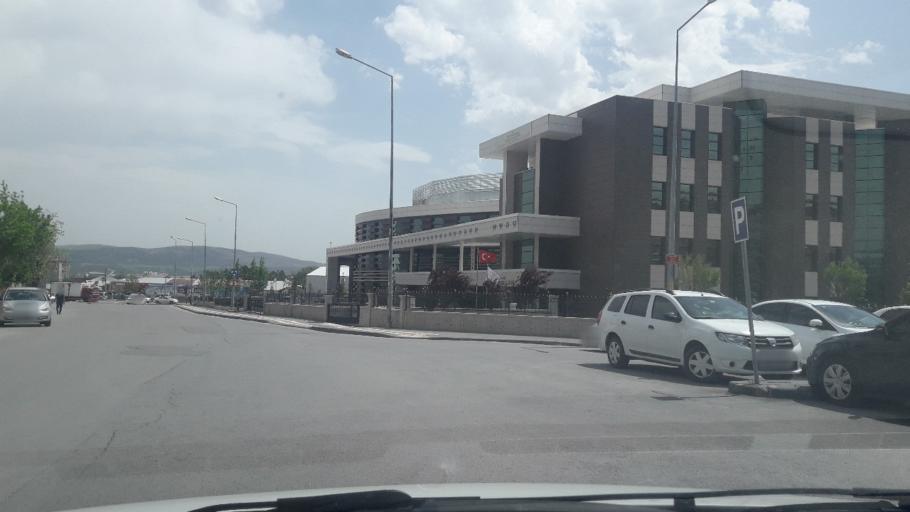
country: TR
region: Sivas
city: Sivas
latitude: 39.7430
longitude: 37.0118
